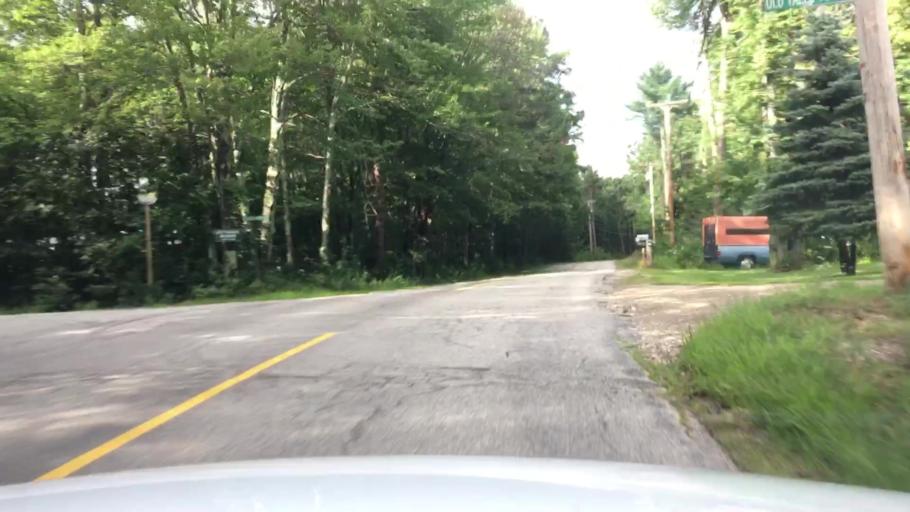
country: US
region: Maine
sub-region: York County
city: West Kennebunk
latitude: 43.4203
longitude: -70.6568
